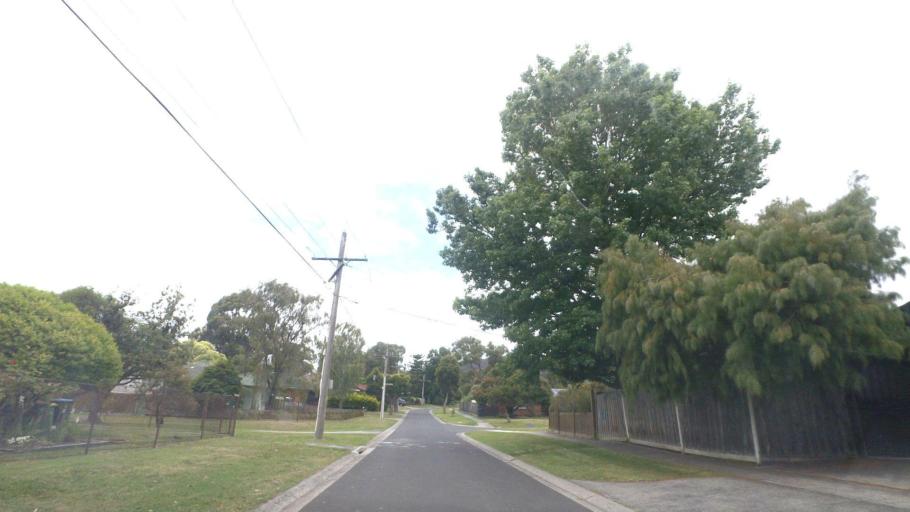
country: AU
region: Victoria
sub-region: Knox
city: The Basin
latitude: -37.8558
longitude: 145.3063
